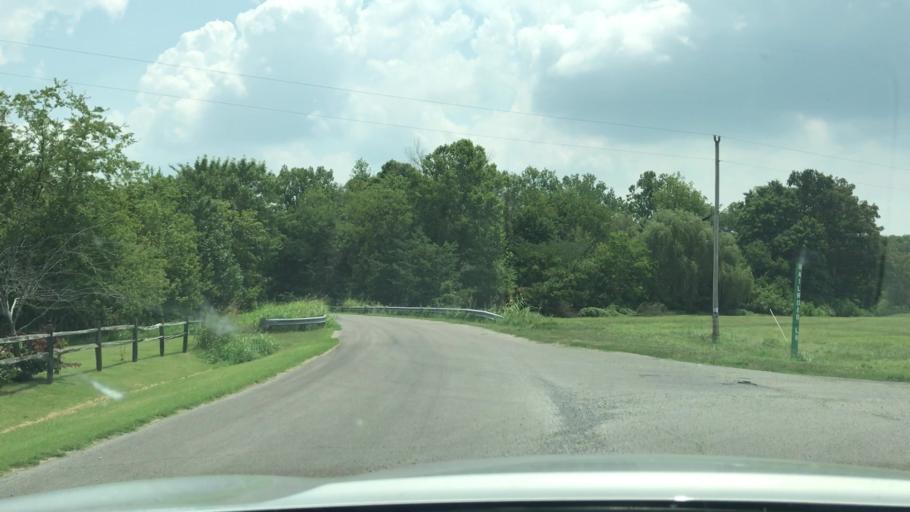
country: US
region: Kentucky
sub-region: Todd County
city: Elkton
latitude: 36.7798
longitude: -87.1502
